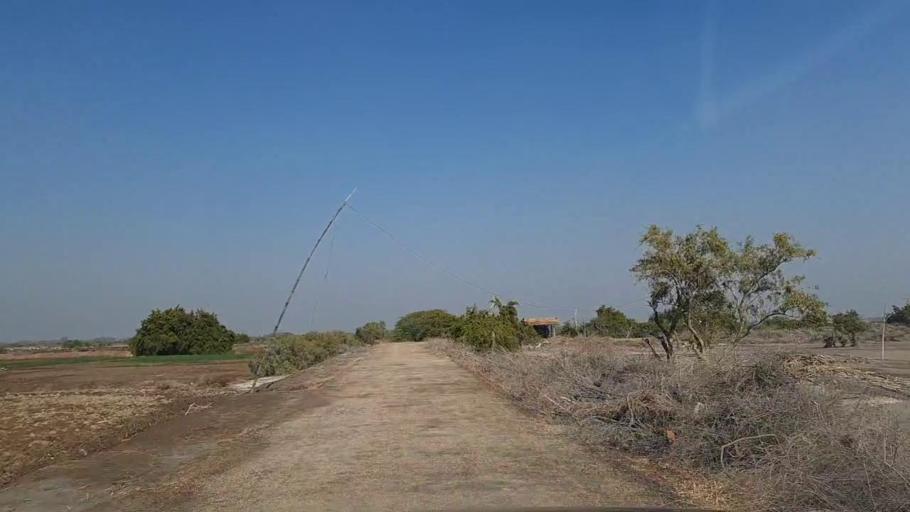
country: PK
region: Sindh
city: Nawabshah
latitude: 26.2975
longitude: 68.3843
